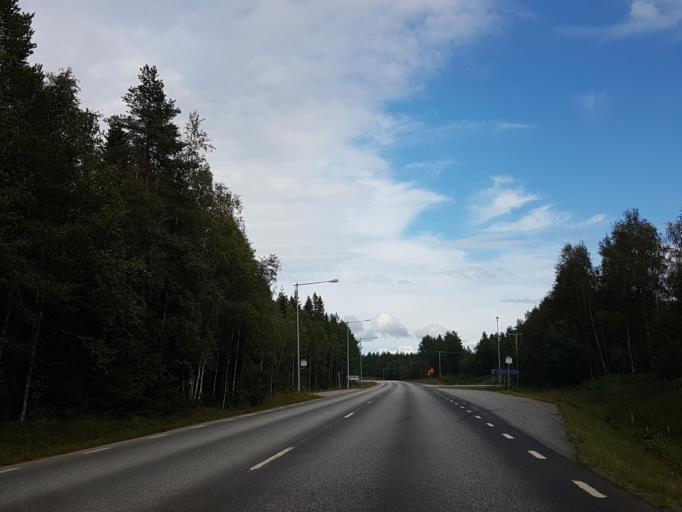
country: SE
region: Vaesterbotten
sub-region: Umea Kommun
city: Taftea
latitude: 63.8159
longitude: 20.4204
